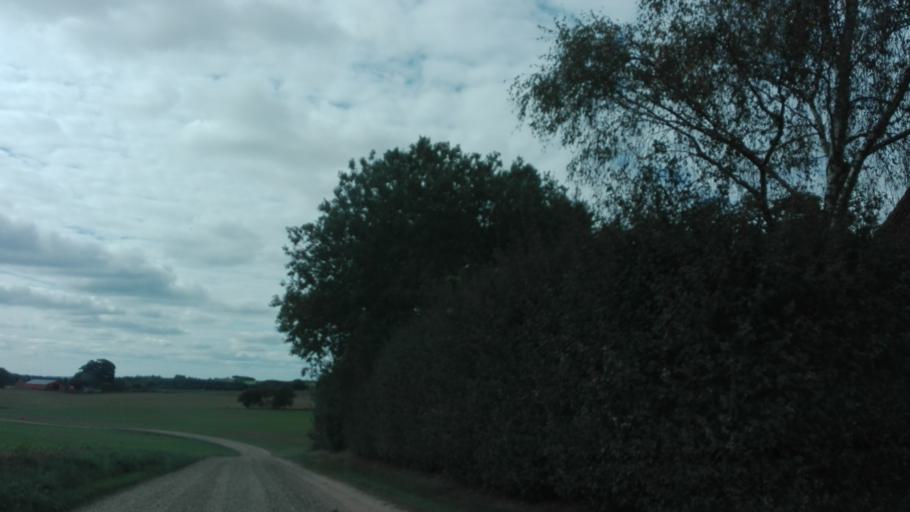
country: DK
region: Central Jutland
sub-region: Skanderborg Kommune
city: Stilling
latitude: 56.0870
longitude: 10.0027
